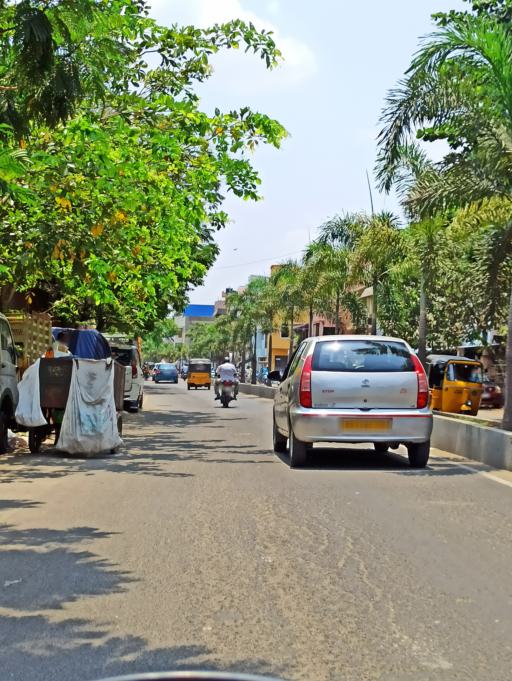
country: IN
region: Tamil Nadu
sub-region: Chennai
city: Chetput
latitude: 13.0929
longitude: 80.2336
